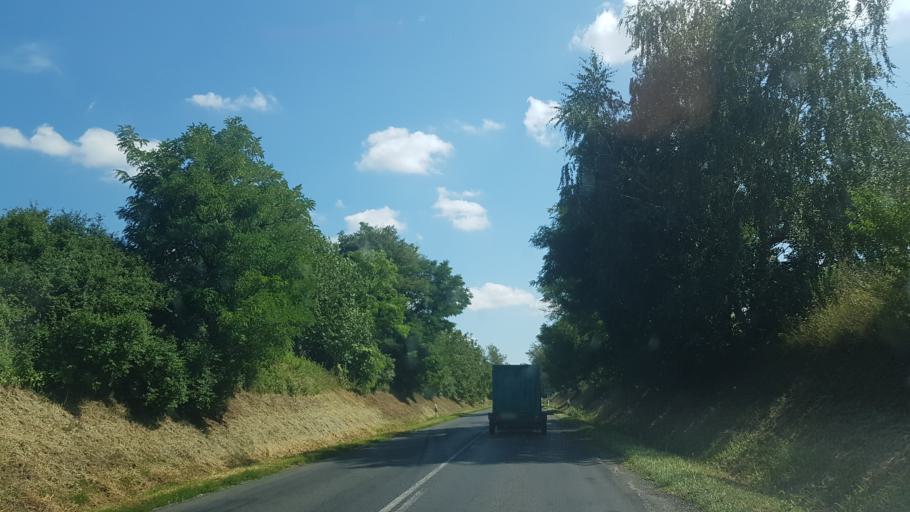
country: HU
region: Somogy
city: Bohonye
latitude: 46.4520
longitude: 17.3721
